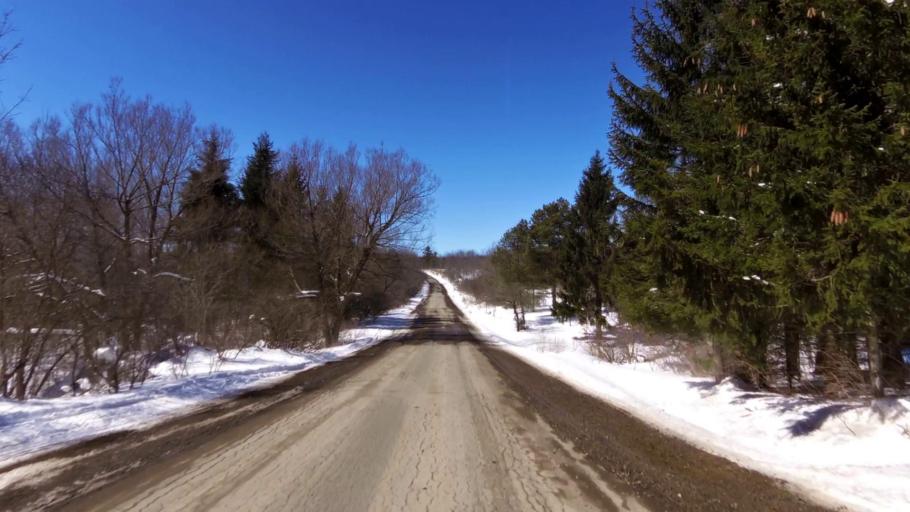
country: US
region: New York
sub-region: Allegany County
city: Houghton
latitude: 42.4126
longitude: -78.3018
